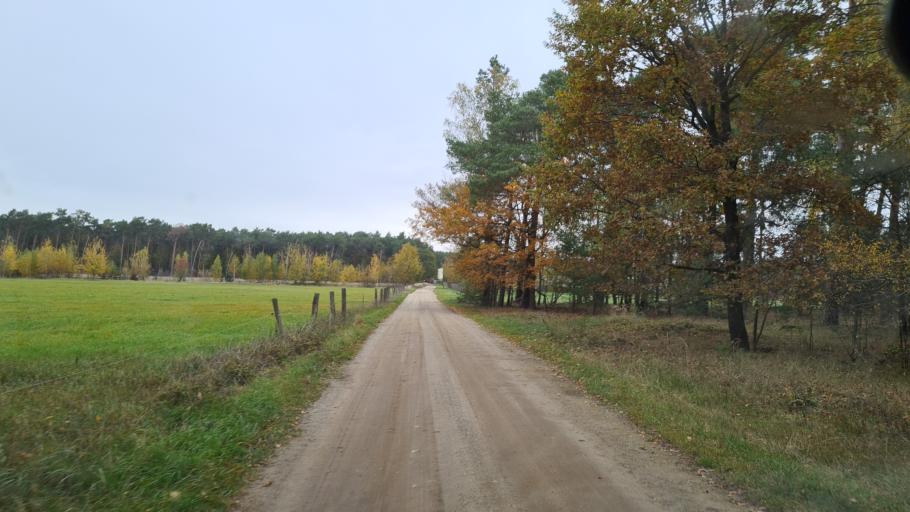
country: DE
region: Brandenburg
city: Finsterwalde
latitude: 51.6506
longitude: 13.7607
